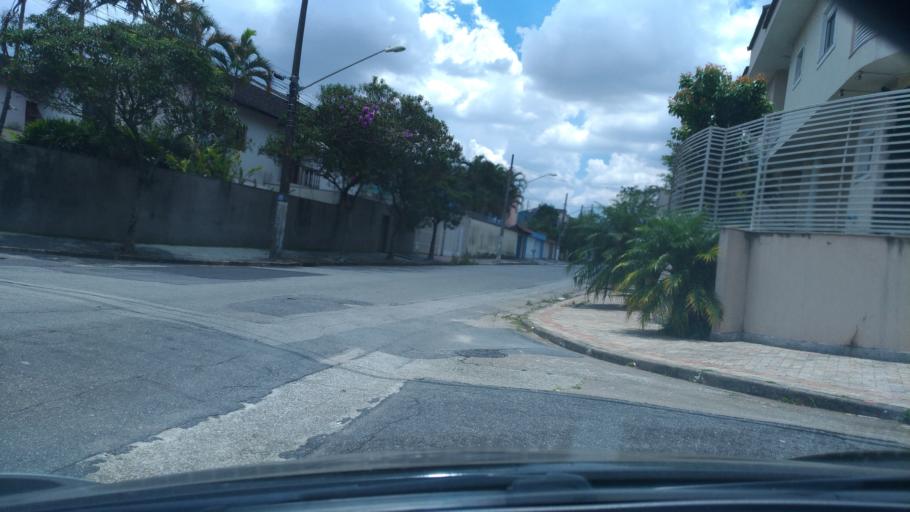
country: BR
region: Sao Paulo
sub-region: Sao Bernardo Do Campo
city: Sao Bernardo do Campo
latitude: -23.7070
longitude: -46.5841
